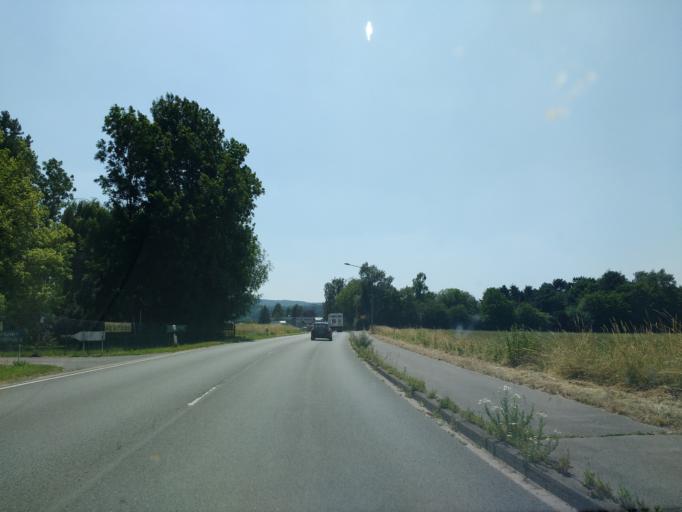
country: DE
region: North Rhine-Westphalia
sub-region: Regierungsbezirk Detmold
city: Detmold
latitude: 51.9225
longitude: 8.9167
